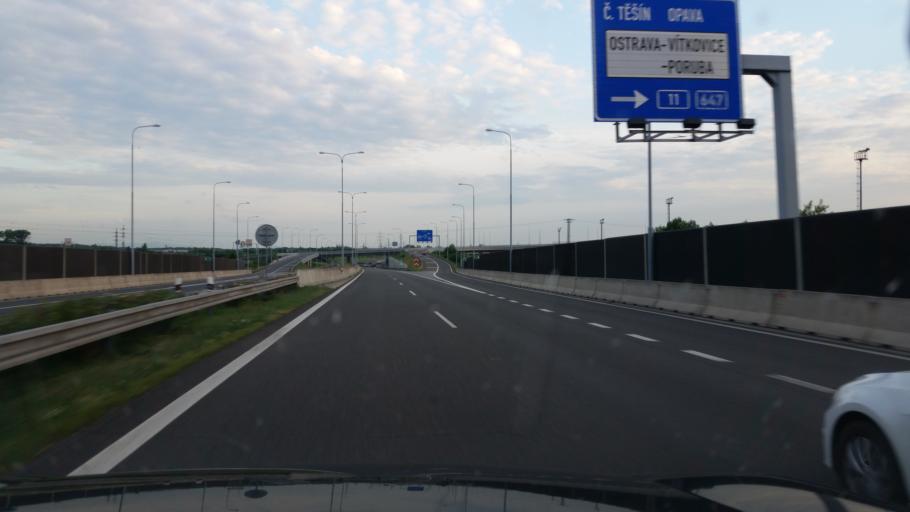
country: CZ
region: Moravskoslezsky
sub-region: Okres Ostrava-Mesto
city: Ostrava
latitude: 49.8147
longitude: 18.2084
